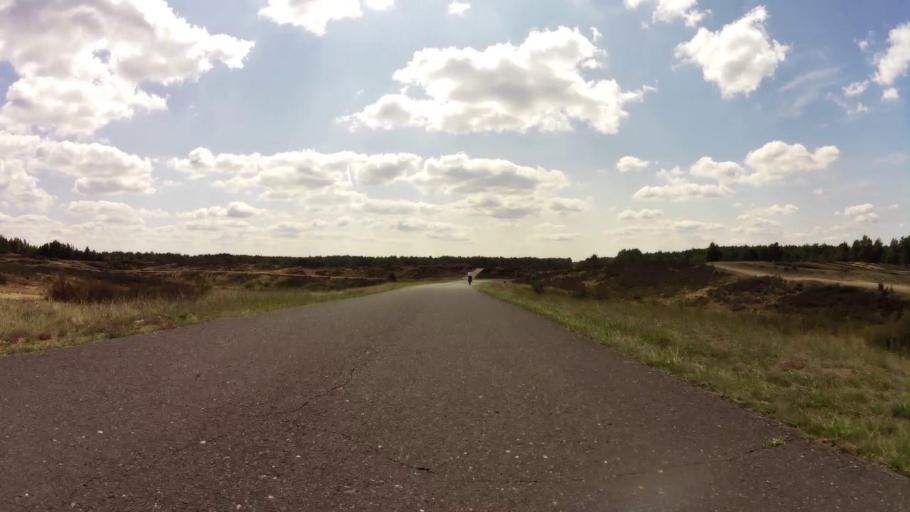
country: PL
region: West Pomeranian Voivodeship
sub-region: Powiat drawski
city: Drawsko Pomorskie
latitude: 53.4138
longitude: 15.7385
